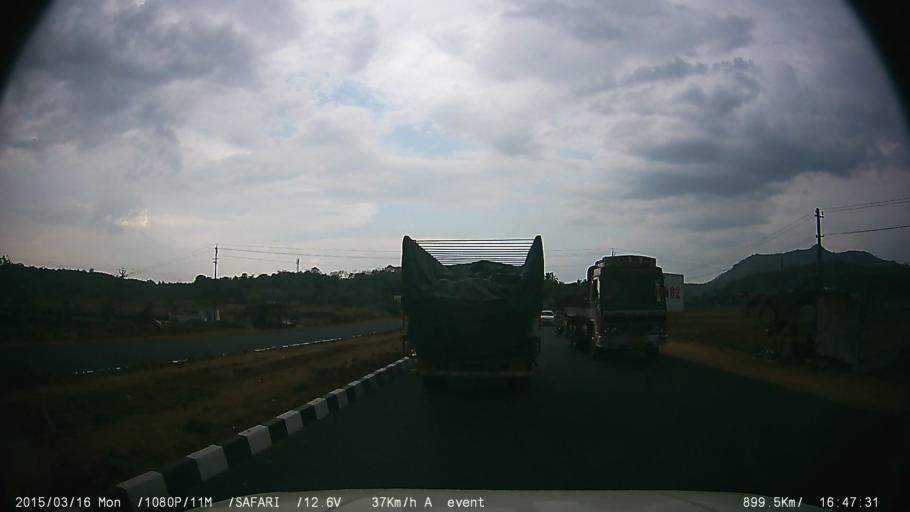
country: IN
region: Kerala
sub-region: Thrissur District
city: Chelakara
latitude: 10.6179
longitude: 76.5062
